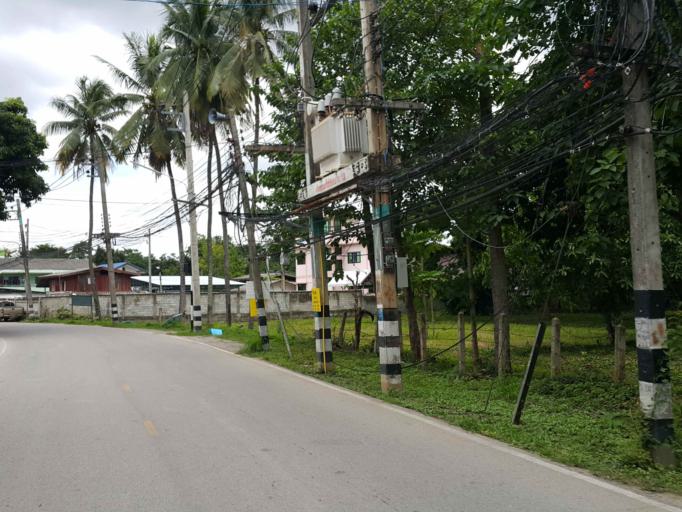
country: TH
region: Chiang Mai
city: Chiang Mai
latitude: 18.8215
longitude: 98.9994
